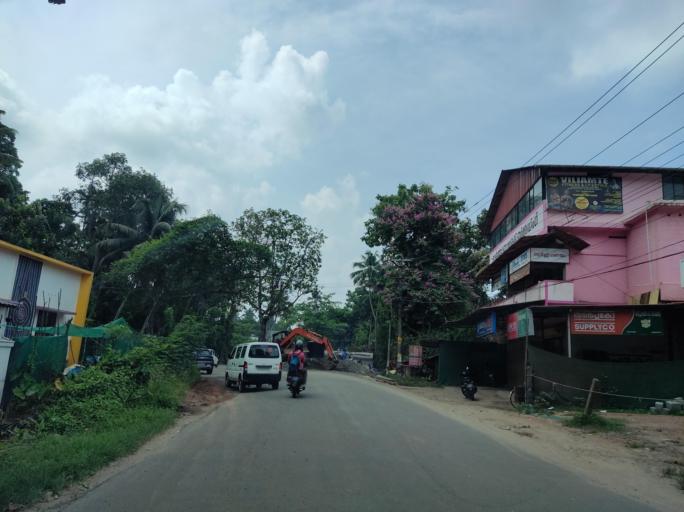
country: IN
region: Kerala
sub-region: Alappuzha
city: Shertallai
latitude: 9.6714
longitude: 76.4221
